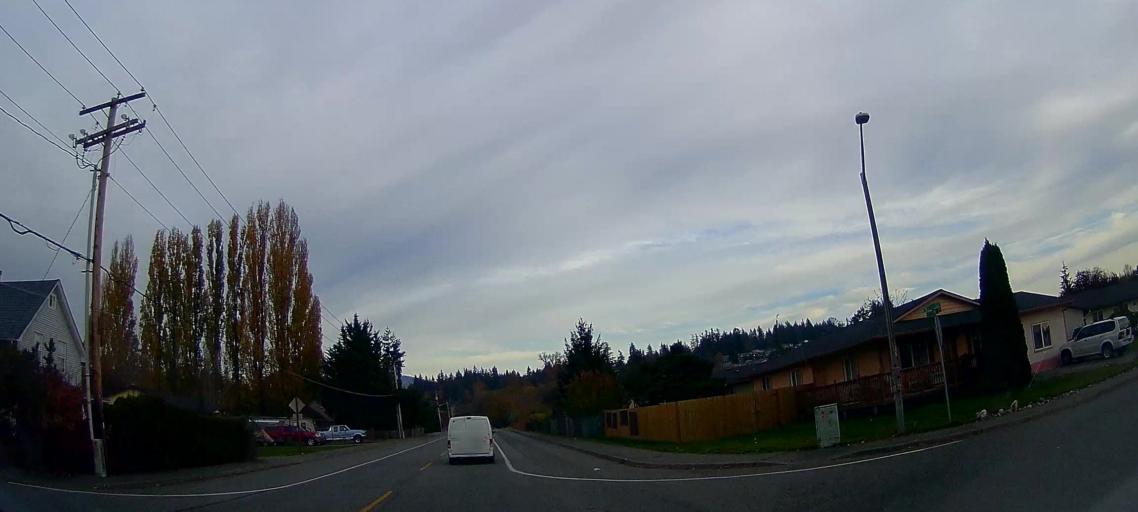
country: US
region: Washington
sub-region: Skagit County
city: Mount Vernon
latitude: 48.4136
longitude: -122.3054
